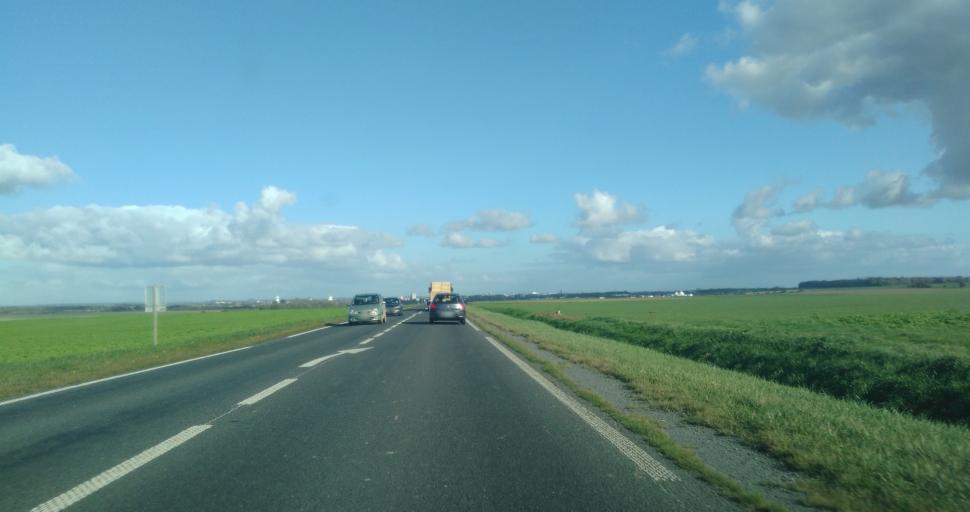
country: FR
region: Nord-Pas-de-Calais
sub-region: Departement du Pas-de-Calais
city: Riviere
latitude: 50.2548
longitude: 2.6843
